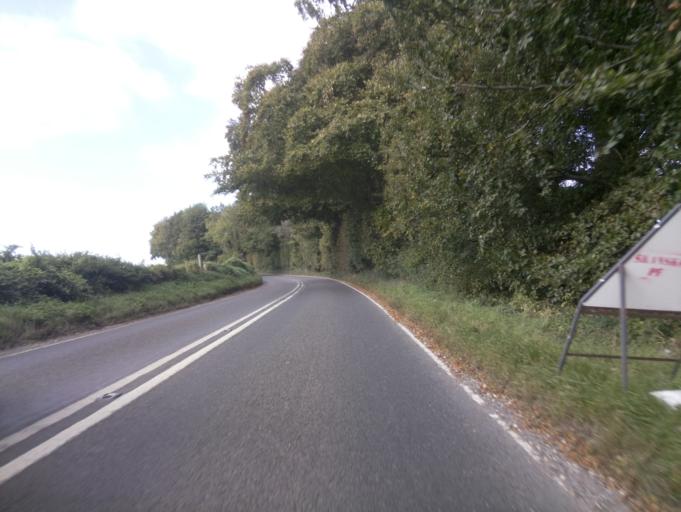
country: GB
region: England
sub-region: Hampshire
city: Basingstoke
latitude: 51.2299
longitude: -1.0648
